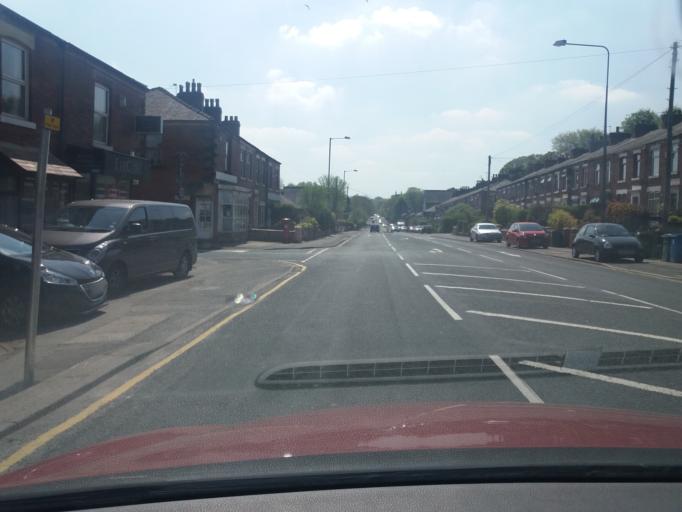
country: GB
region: England
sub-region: Lancashire
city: Clayton-le-Woods
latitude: 53.6939
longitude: -2.6384
